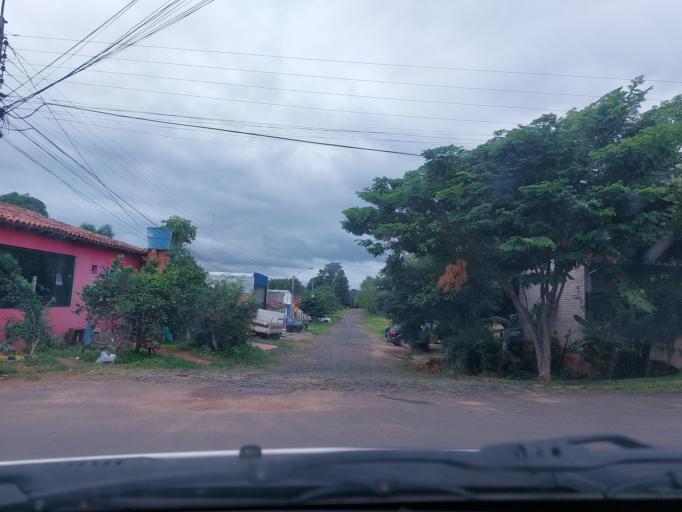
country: PY
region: San Pedro
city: Guayaybi
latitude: -24.6600
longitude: -56.4428
